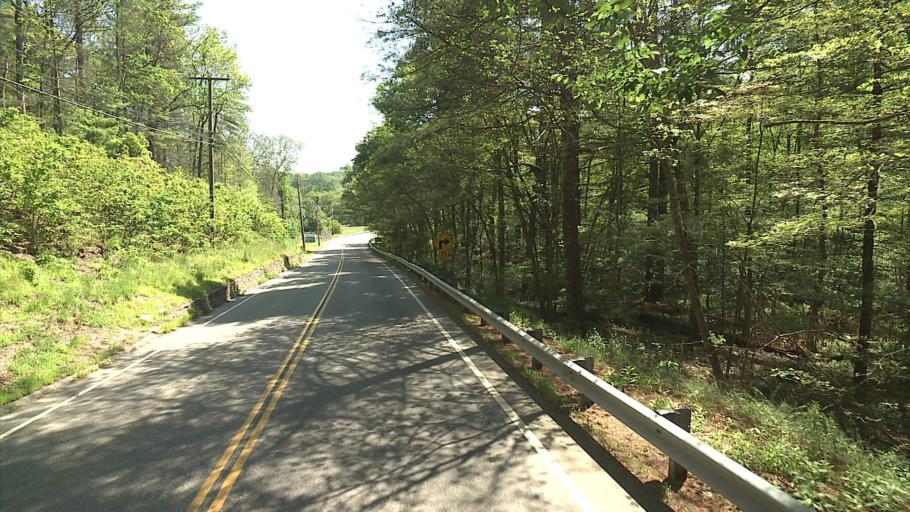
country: US
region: Connecticut
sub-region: Windham County
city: Moosup
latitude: 41.7074
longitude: -71.8352
